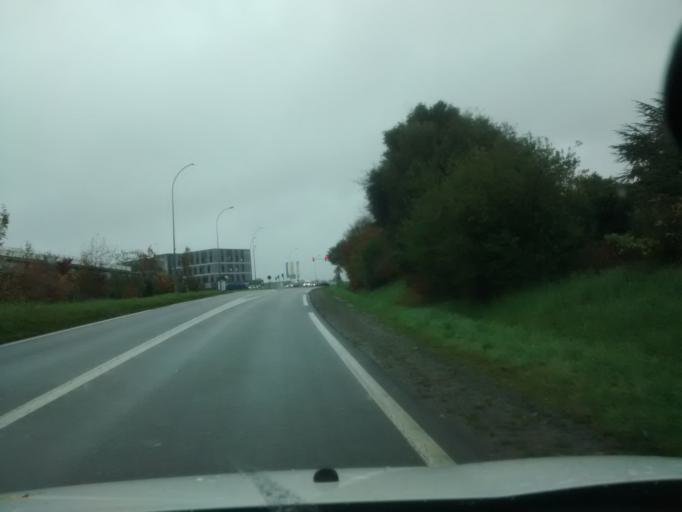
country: FR
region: Brittany
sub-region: Departement d'Ille-et-Vilaine
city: Chantepie
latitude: 48.0864
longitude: -1.6244
